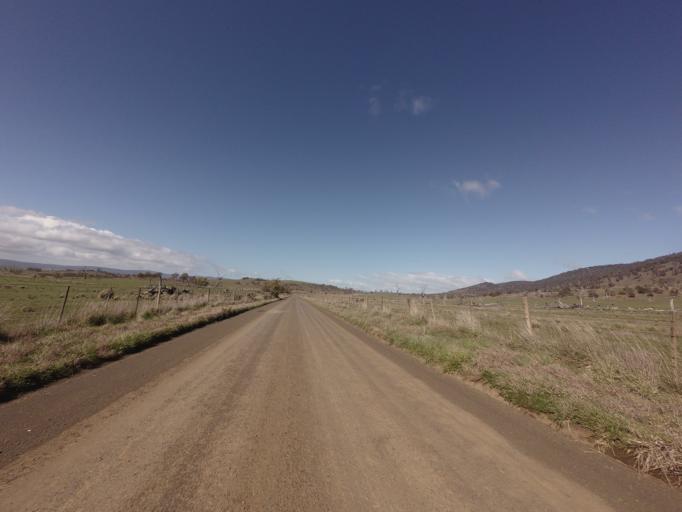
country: AU
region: Tasmania
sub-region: Northern Midlands
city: Evandale
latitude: -41.9262
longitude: 147.4100
